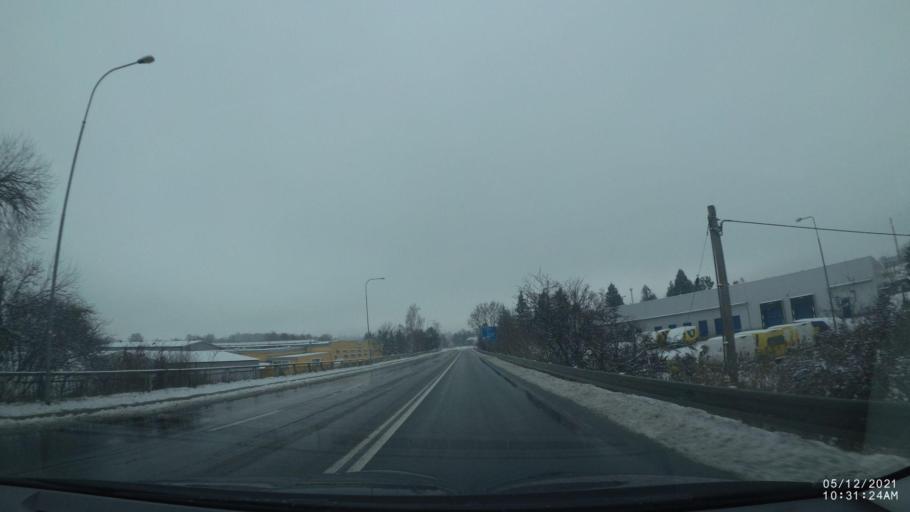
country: CZ
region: Kralovehradecky
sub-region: Okres Rychnov nad Kneznou
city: Rychnov nad Kneznou
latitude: 50.1521
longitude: 16.2821
